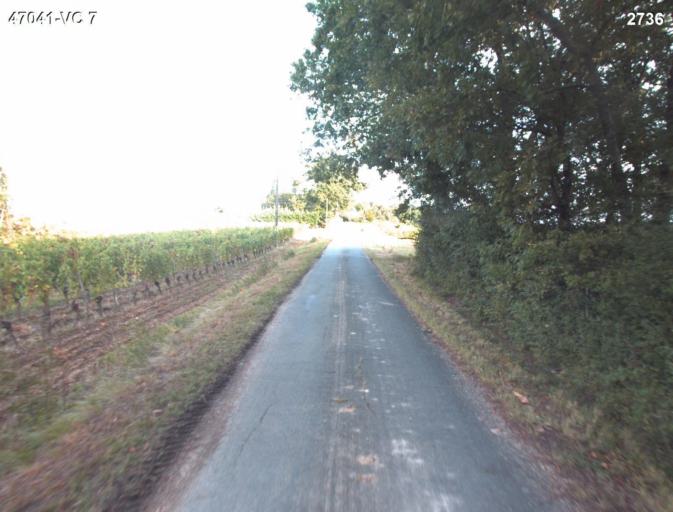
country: FR
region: Aquitaine
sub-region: Departement du Lot-et-Garonne
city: Port-Sainte-Marie
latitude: 44.1872
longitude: 0.4244
